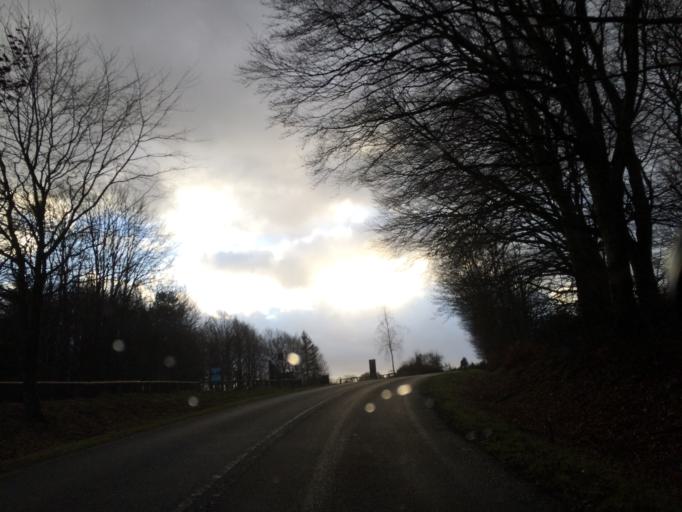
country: DK
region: Central Jutland
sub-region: Silkeborg Kommune
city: Svejbaek
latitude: 56.1011
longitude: 9.6852
